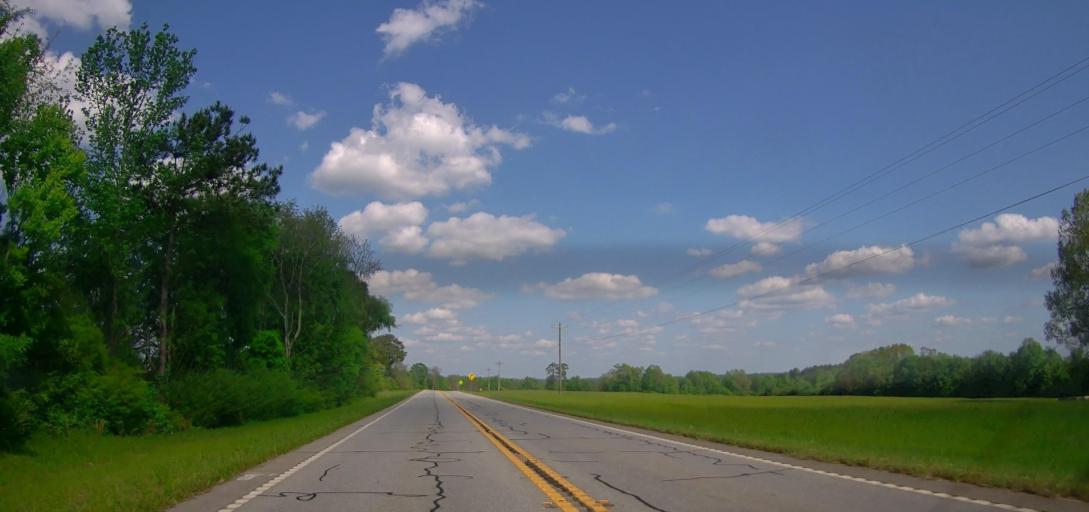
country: US
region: Georgia
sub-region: Greene County
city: Greensboro
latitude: 33.5963
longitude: -83.2965
